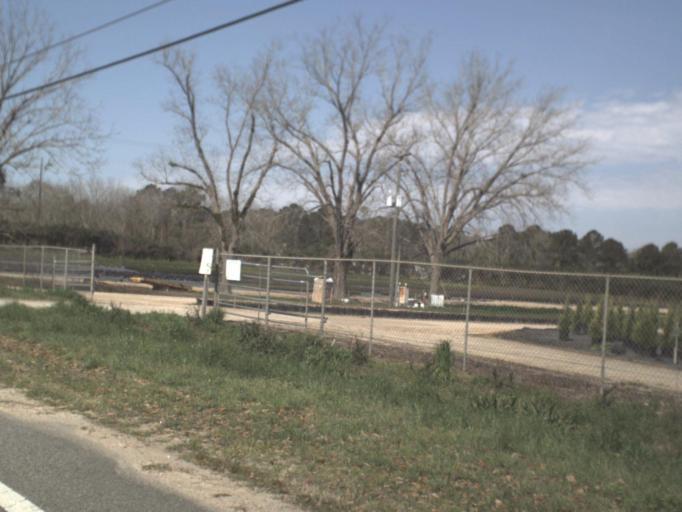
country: US
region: Florida
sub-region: Gadsden County
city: Havana
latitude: 30.6200
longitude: -84.4321
